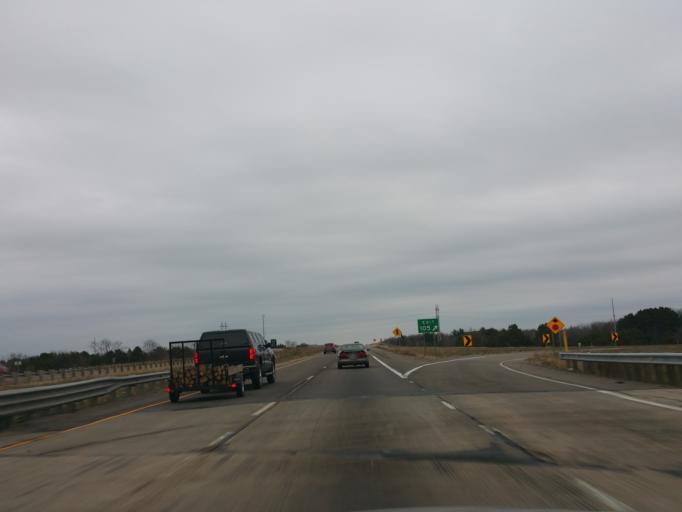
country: US
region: Wisconsin
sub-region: Jackson County
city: Black River Falls
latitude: 44.3887
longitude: -91.0061
